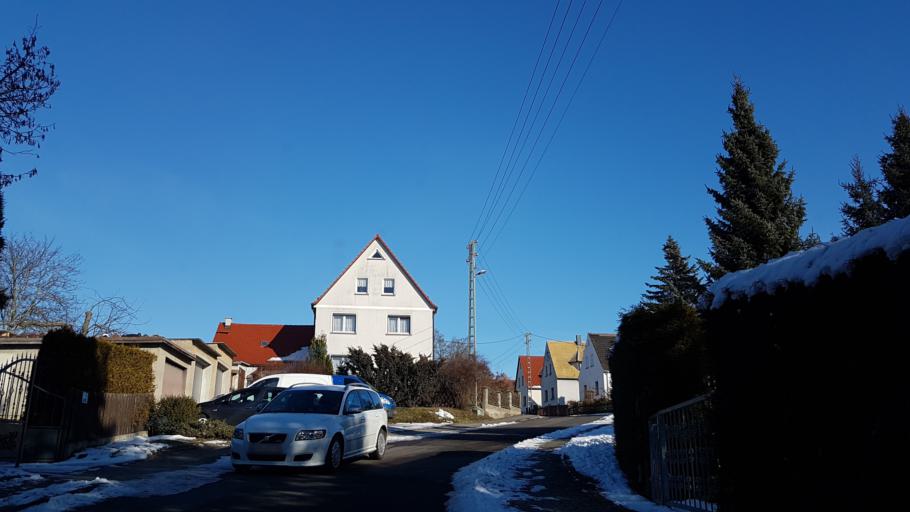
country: DE
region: Thuringia
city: Nobitz
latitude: 50.9706
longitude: 12.5014
